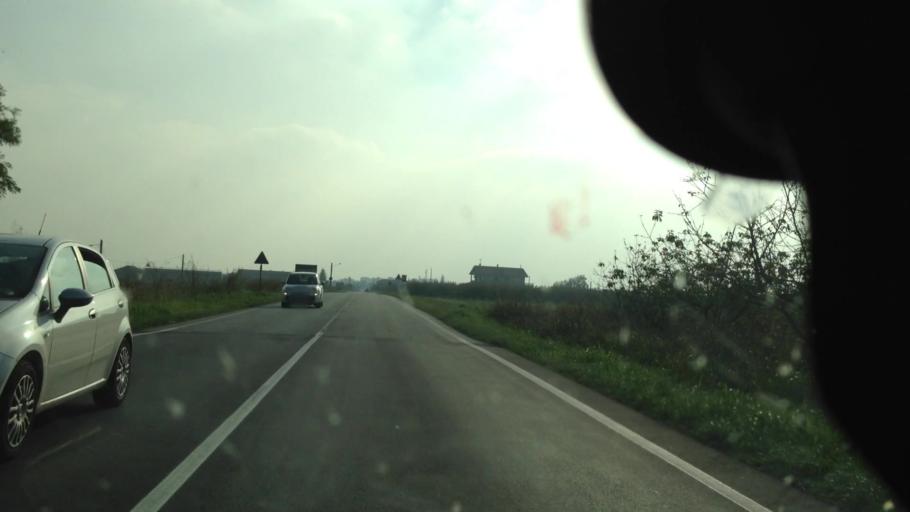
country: IT
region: Piedmont
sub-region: Provincia di Vercelli
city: Borgo d'Ale
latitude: 45.3293
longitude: 8.0381
